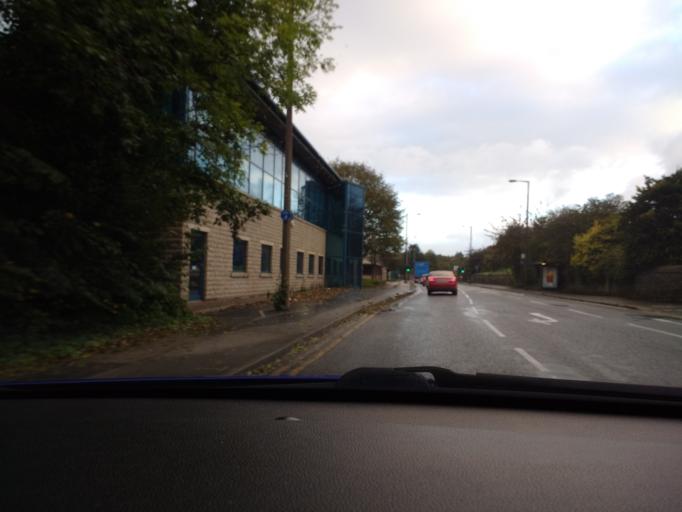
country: GB
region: England
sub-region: Lancashire
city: Bolton le Sands
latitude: 54.0669
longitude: -2.7845
